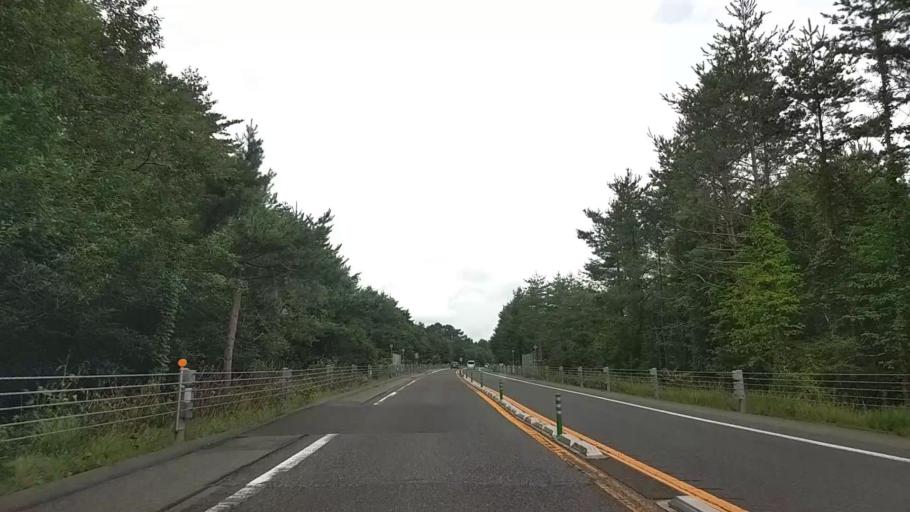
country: JP
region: Yamanashi
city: Fujikawaguchiko
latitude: 35.4569
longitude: 138.7850
